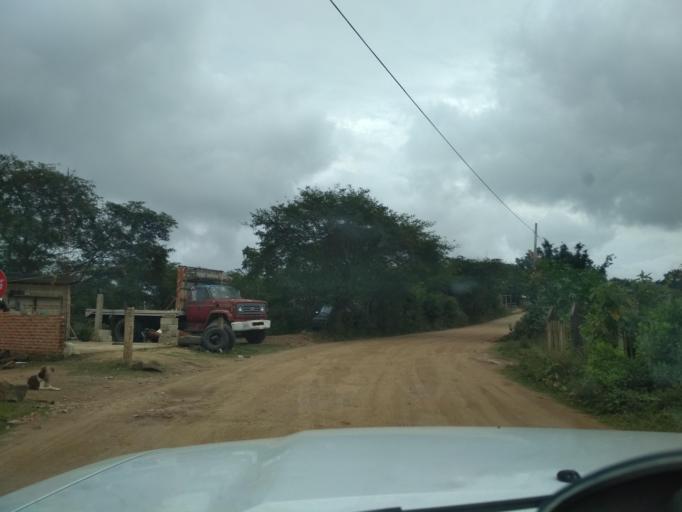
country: MX
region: Veracruz
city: El Castillo
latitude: 19.5469
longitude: -96.8503
